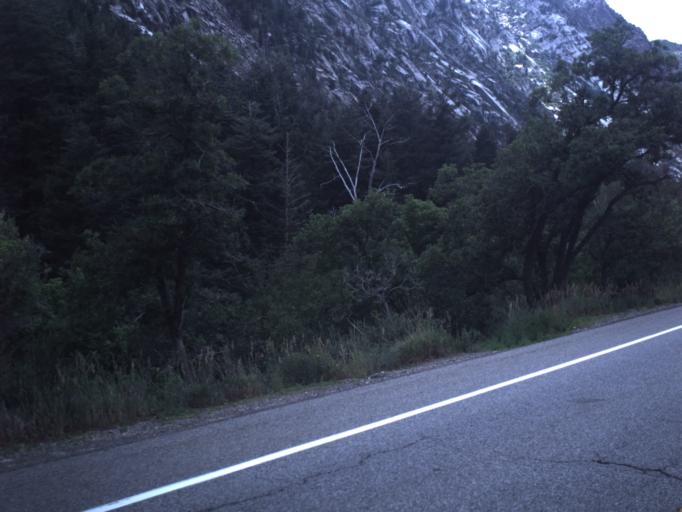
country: US
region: Utah
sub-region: Salt Lake County
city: Granite
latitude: 40.5716
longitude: -111.7535
